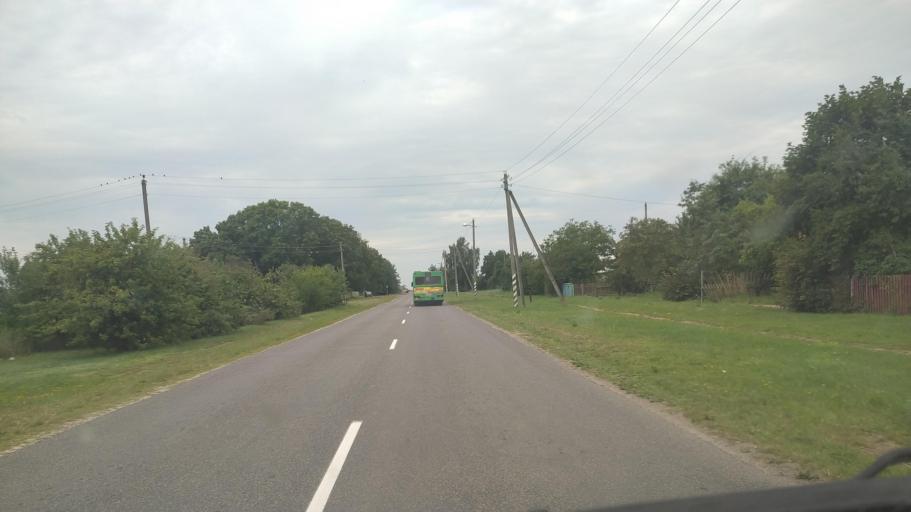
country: BY
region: Brest
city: Byaroza
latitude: 52.5808
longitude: 24.8592
